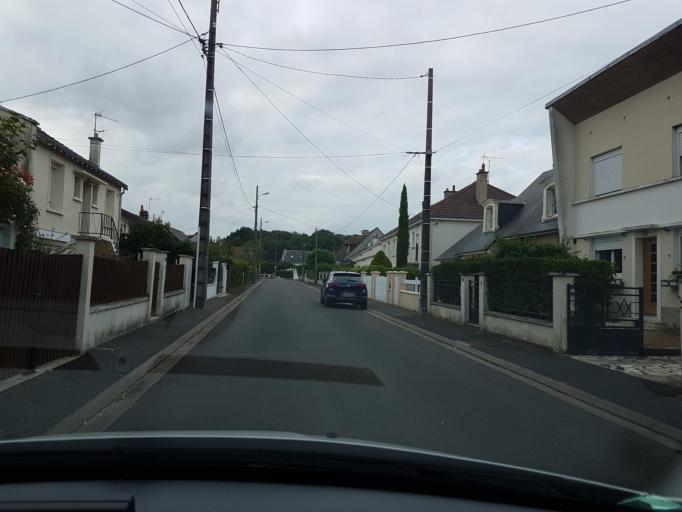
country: FR
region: Centre
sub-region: Departement d'Indre-et-Loire
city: Saint-Avertin
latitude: 47.3651
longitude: 0.7497
